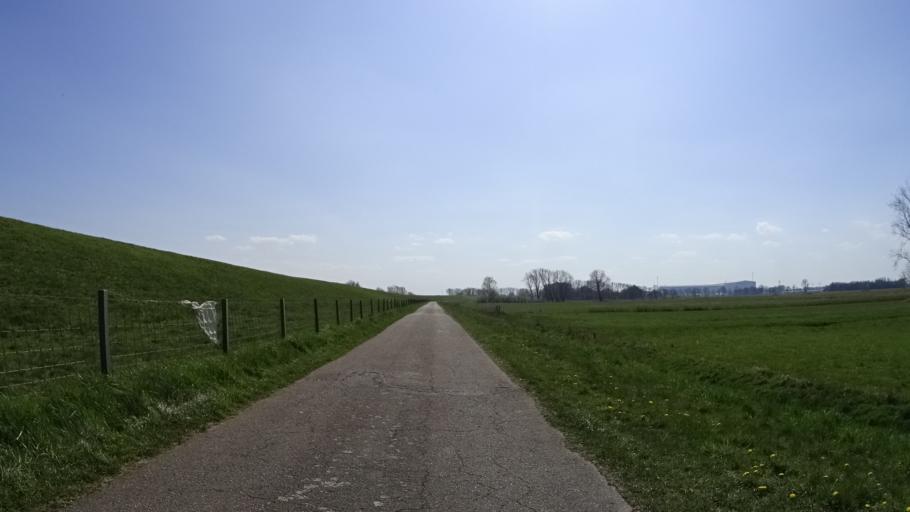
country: DE
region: Lower Saxony
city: Weener
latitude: 53.1245
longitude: 7.3708
